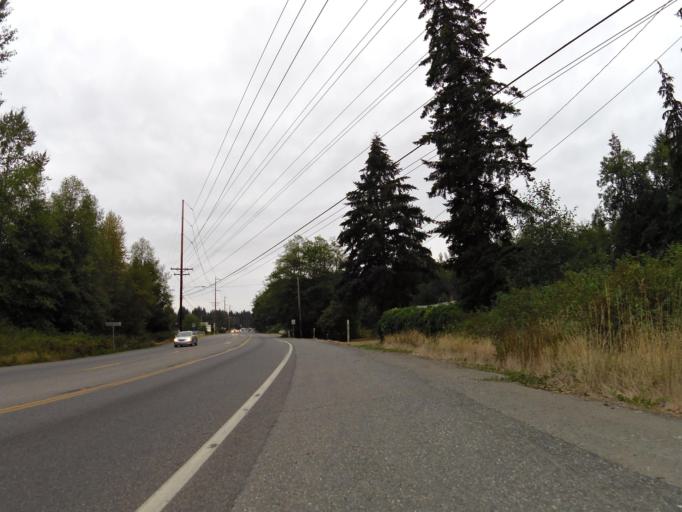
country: US
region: Washington
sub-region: Jefferson County
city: Port Hadlock-Irondale
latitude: 48.0429
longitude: -122.7928
